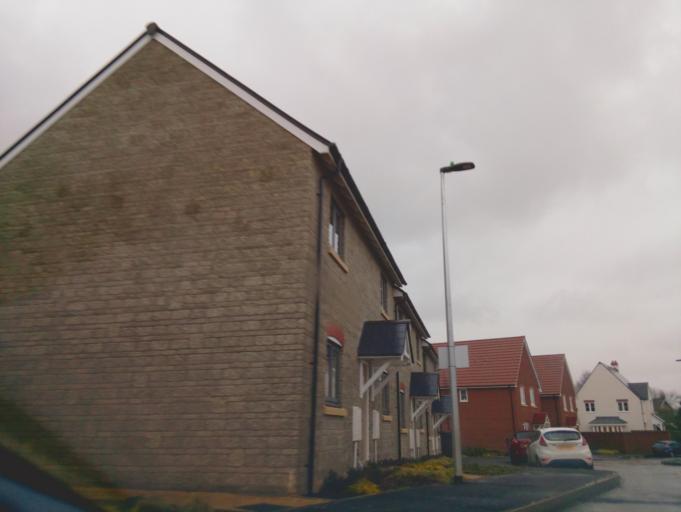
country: GB
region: England
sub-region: South Gloucestershire
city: Charfield
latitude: 51.6293
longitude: -2.3936
